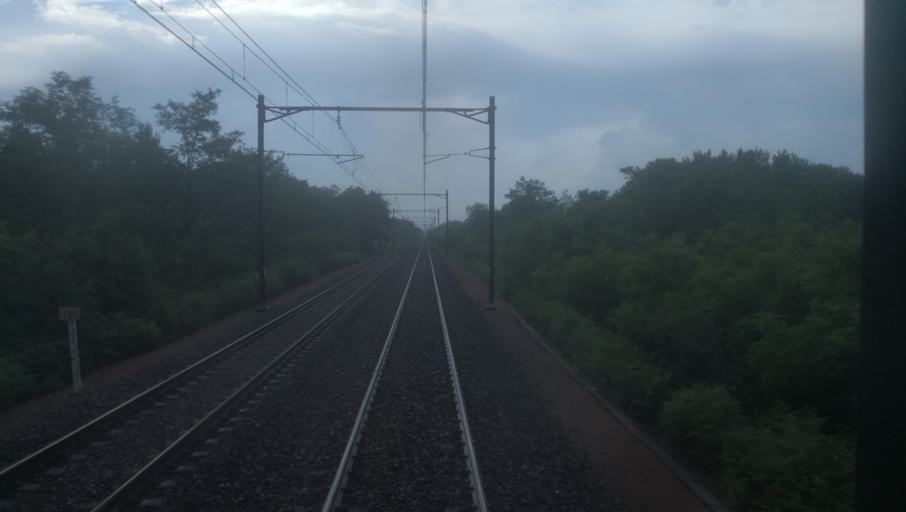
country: FR
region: Centre
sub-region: Departement du Loiret
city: La Ferte-Saint-Aubin
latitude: 47.6645
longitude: 1.9692
